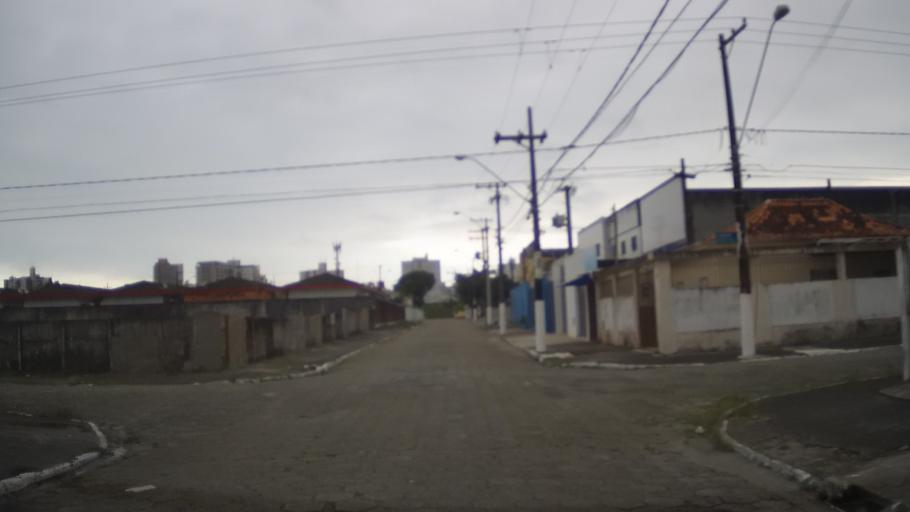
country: BR
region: Sao Paulo
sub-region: Praia Grande
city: Praia Grande
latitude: -24.0013
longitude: -46.4231
